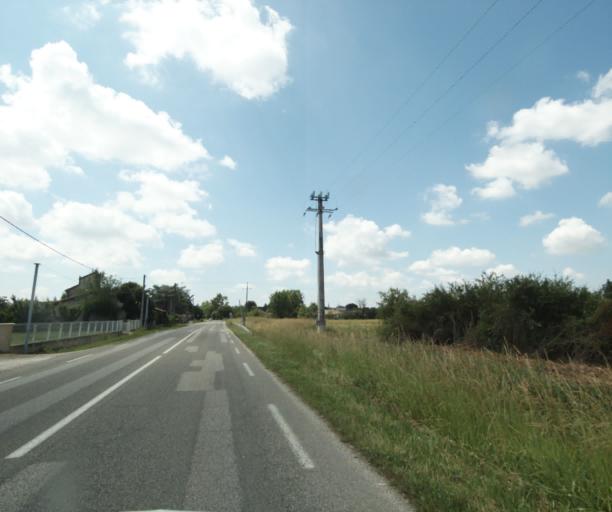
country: FR
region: Midi-Pyrenees
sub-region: Departement du Tarn-et-Garonne
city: Montauban
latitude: 44.0568
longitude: 1.3597
